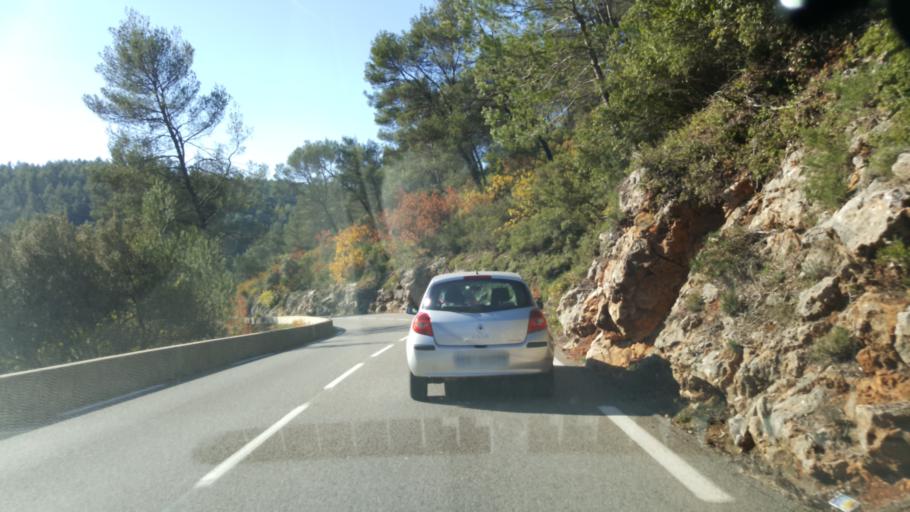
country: FR
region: Provence-Alpes-Cote d'Azur
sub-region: Departement du Var
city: Saint-Zacharie
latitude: 43.3831
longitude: 5.7406
